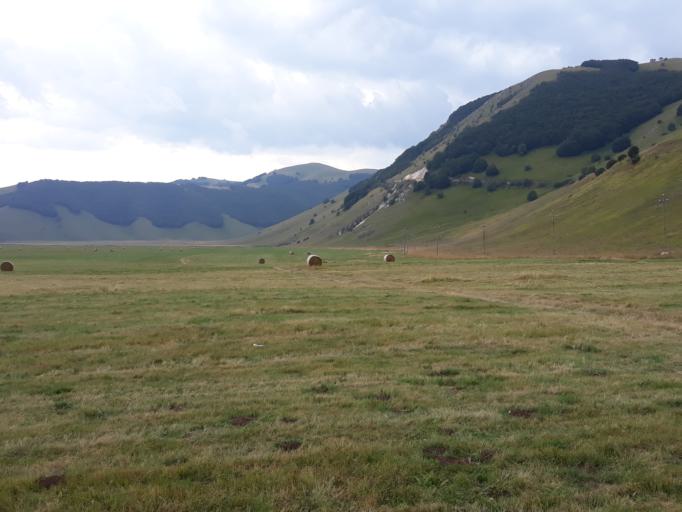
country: IT
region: Umbria
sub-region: Provincia di Perugia
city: Norcia
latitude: 42.7919
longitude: 13.1841
